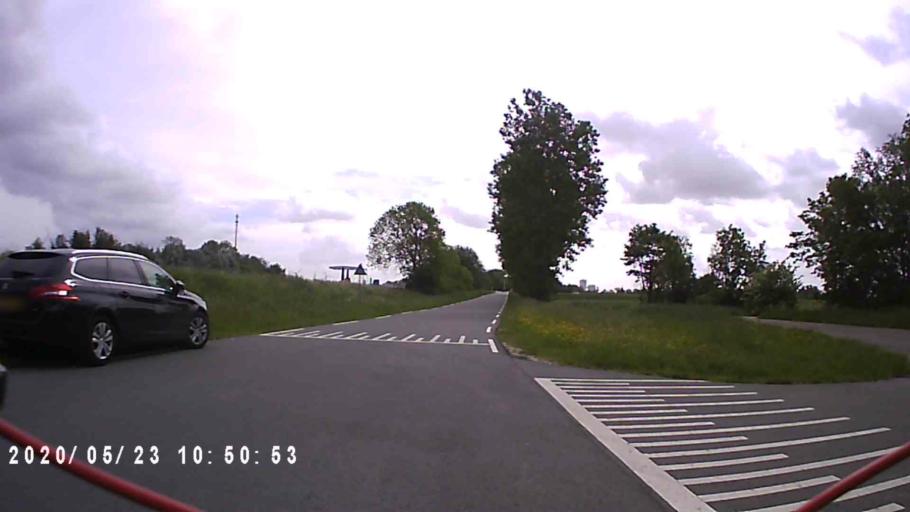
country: NL
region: Groningen
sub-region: Gemeente Delfzijl
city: Delfzijl
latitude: 53.3145
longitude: 6.9370
